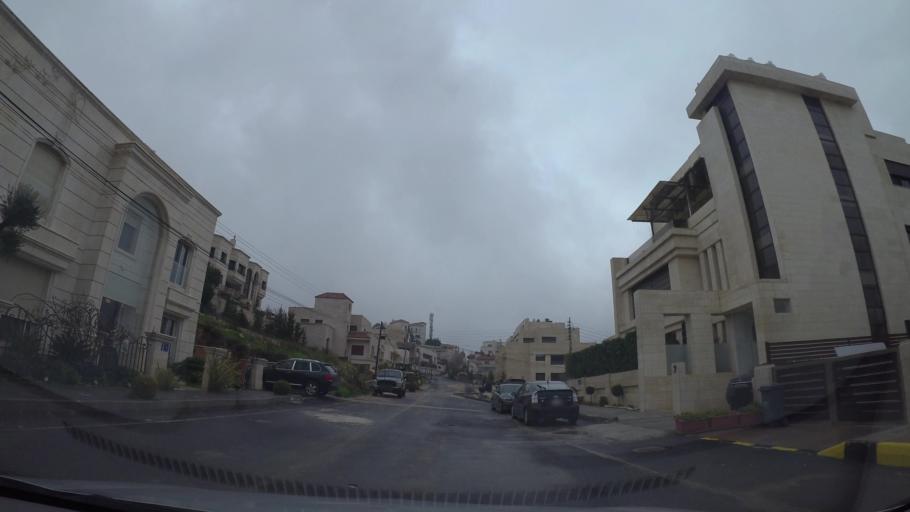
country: JO
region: Amman
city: Al Jubayhah
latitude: 32.0029
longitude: 35.8191
